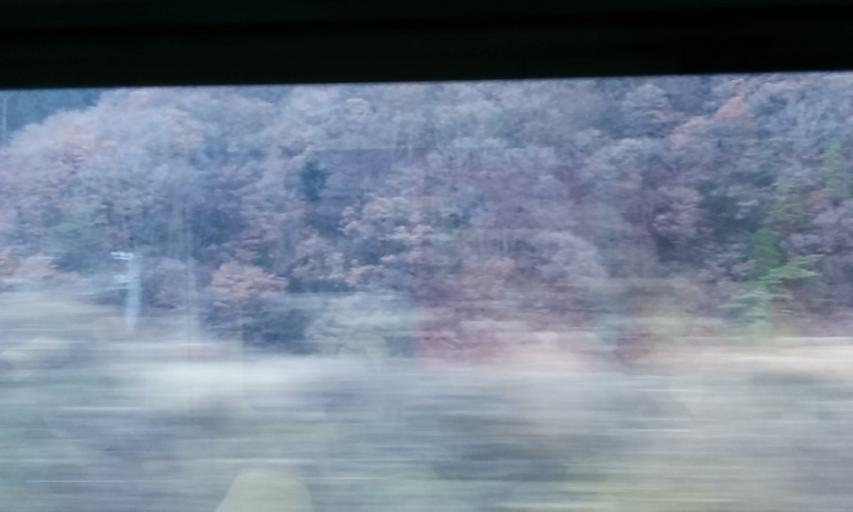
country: JP
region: Nagano
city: Iida
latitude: 35.7305
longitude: 137.7122
